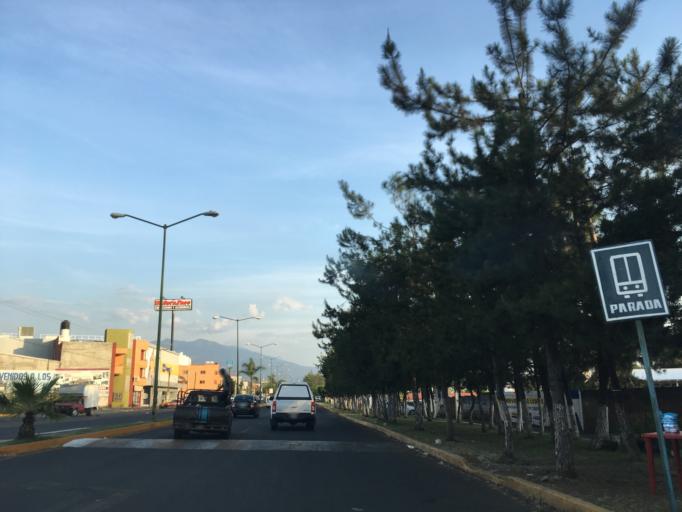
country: MX
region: Michoacan
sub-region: Los Reyes
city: La Higuerita (Colonia San Rafael)
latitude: 19.6000
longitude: -102.4756
